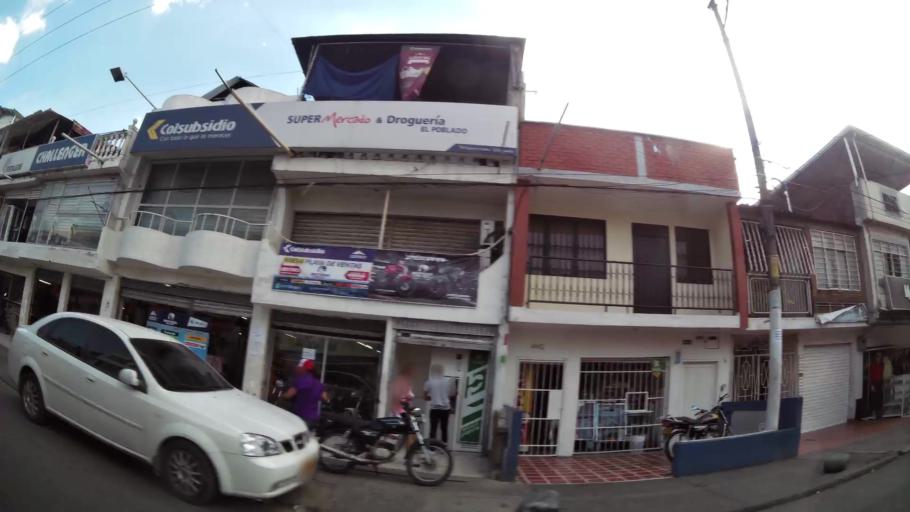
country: CO
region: Valle del Cauca
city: Cali
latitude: 3.4193
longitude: -76.4976
